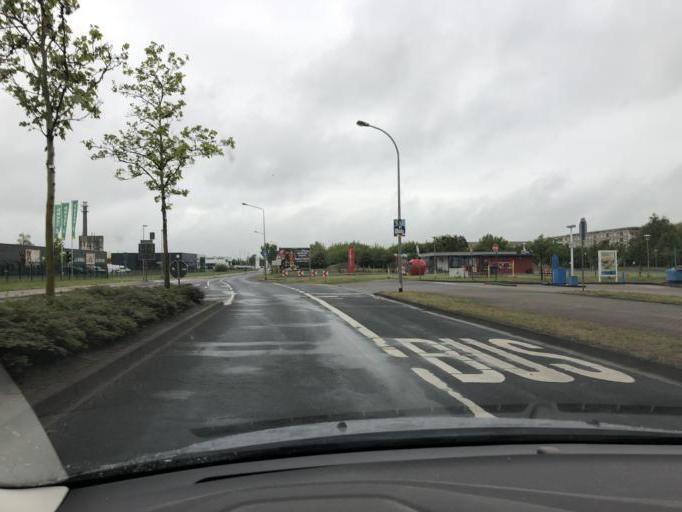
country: DE
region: Saxony-Anhalt
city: Dessau
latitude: 51.8263
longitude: 12.2151
